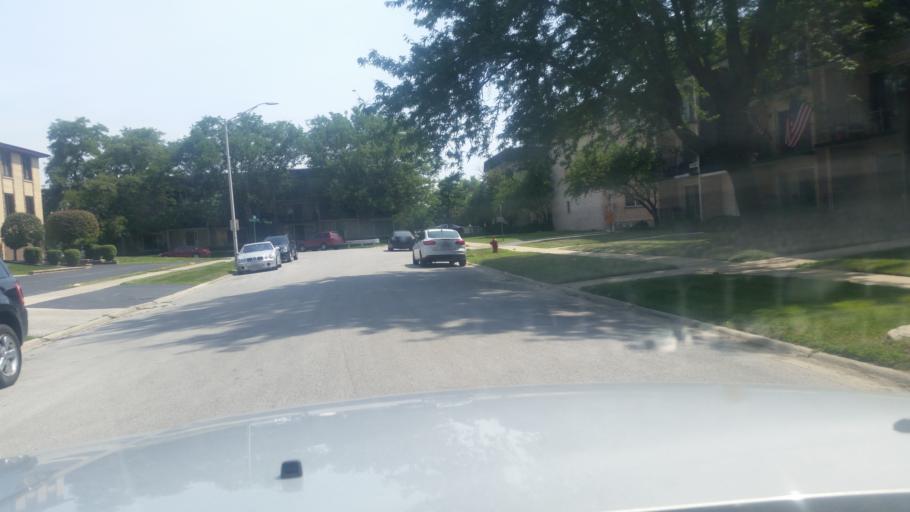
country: US
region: Illinois
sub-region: Cook County
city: Oak Lawn
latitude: 41.7037
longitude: -87.7610
